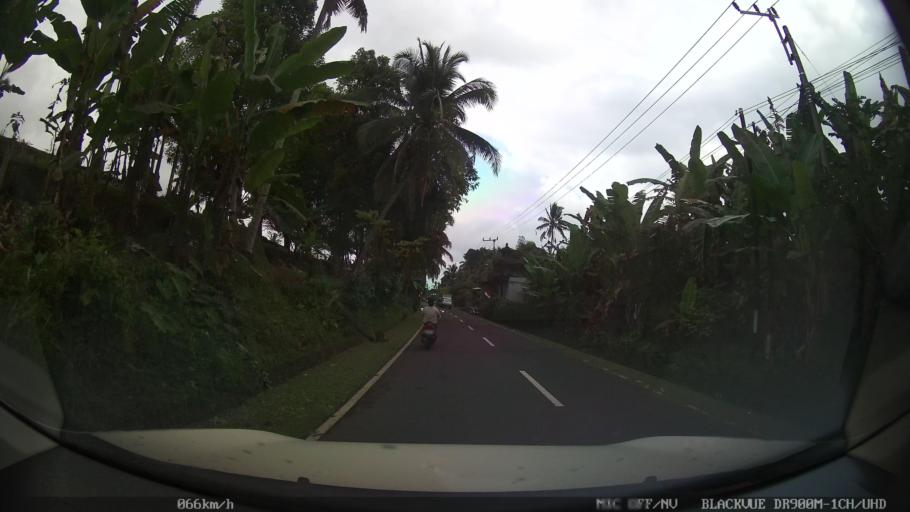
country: ID
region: Bali
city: Penebel
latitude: -8.4126
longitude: 115.1452
